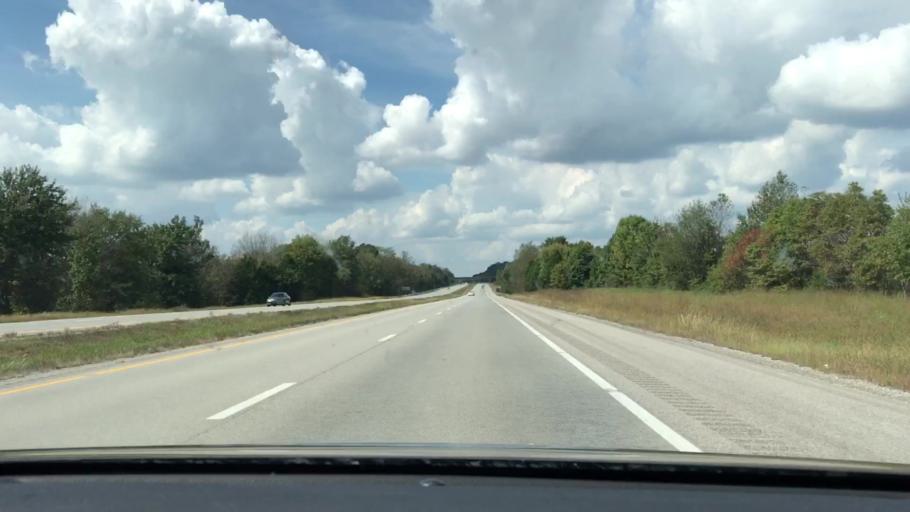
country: US
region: Kentucky
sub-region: Barren County
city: Cave City
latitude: 37.0323
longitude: -86.0525
